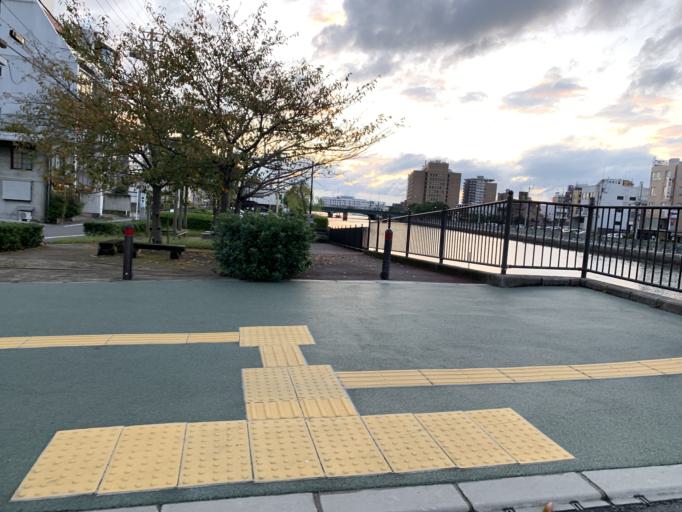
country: JP
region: Tokushima
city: Tokushima-shi
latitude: 34.0677
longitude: 134.5538
